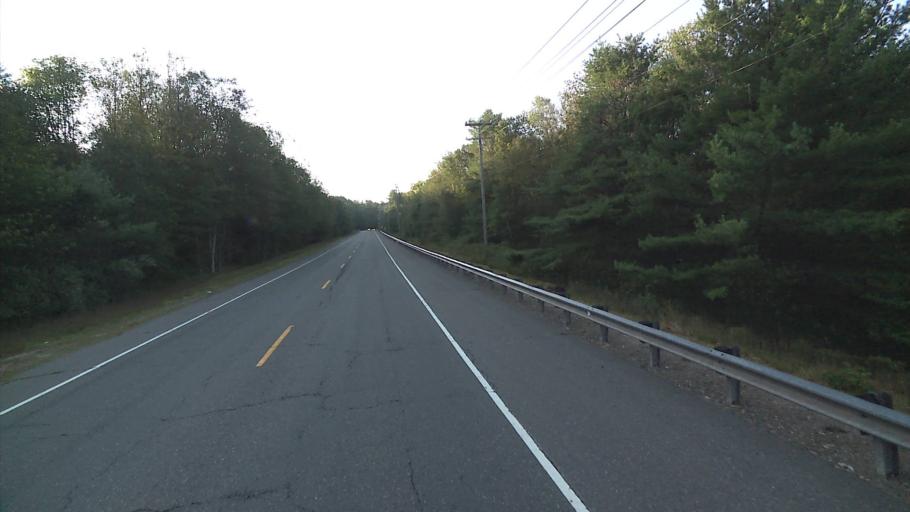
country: US
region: Connecticut
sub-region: Tolland County
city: Stafford Springs
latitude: 41.9094
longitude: -72.2926
